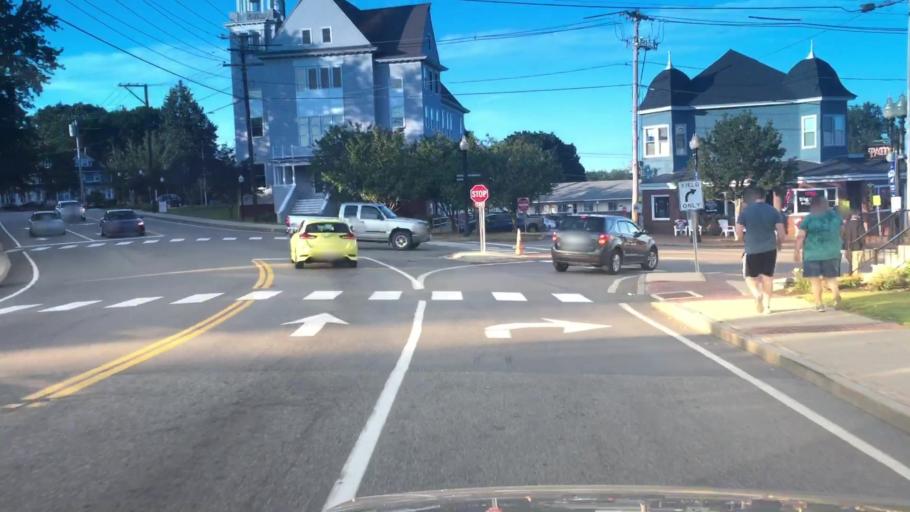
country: US
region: Maine
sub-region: York County
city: Old Orchard Beach
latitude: 43.5171
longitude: -70.3777
